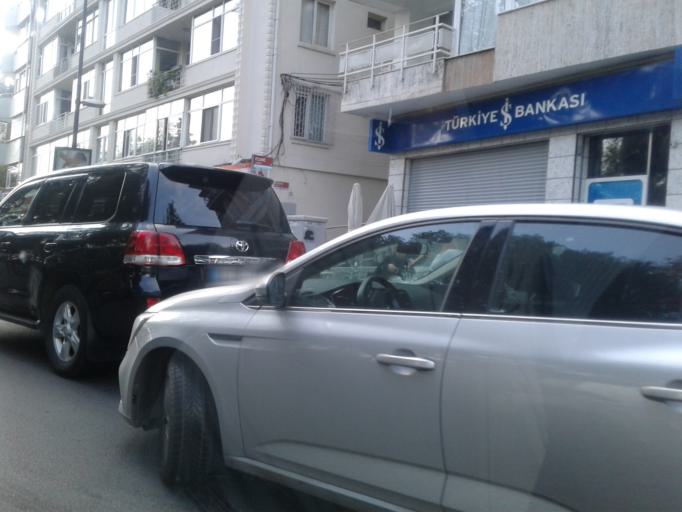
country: TR
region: Istanbul
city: UEskuedar
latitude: 41.0764
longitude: 29.0430
